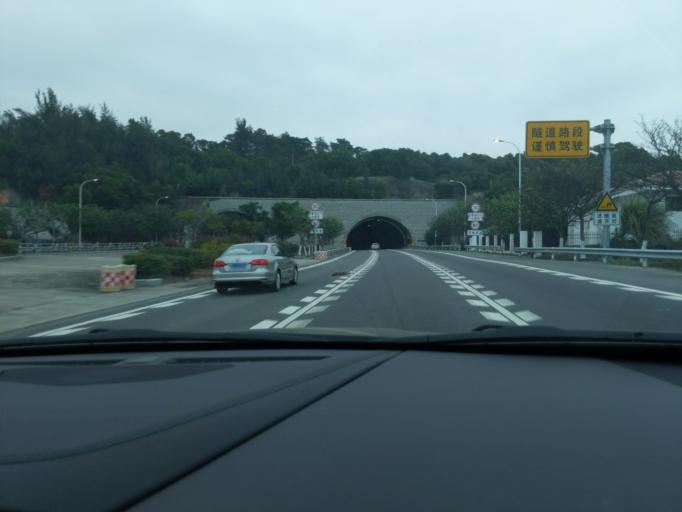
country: CN
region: Fujian
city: Shishi
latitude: 24.7502
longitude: 118.5987
